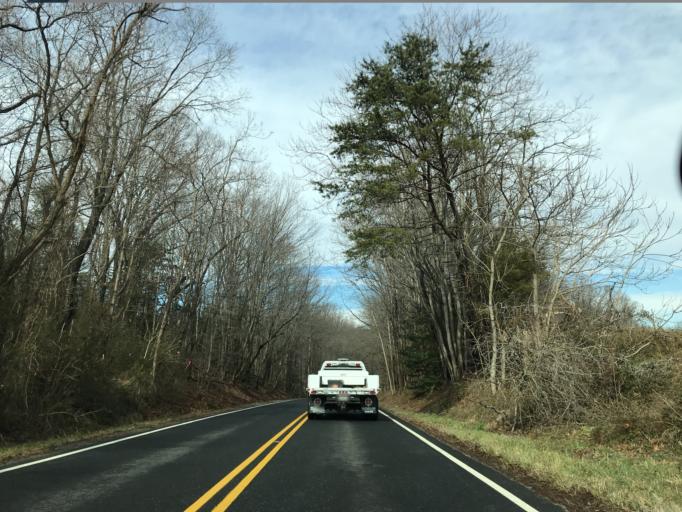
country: US
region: Virginia
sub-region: King George County
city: Dahlgren
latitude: 38.2950
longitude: -77.0683
